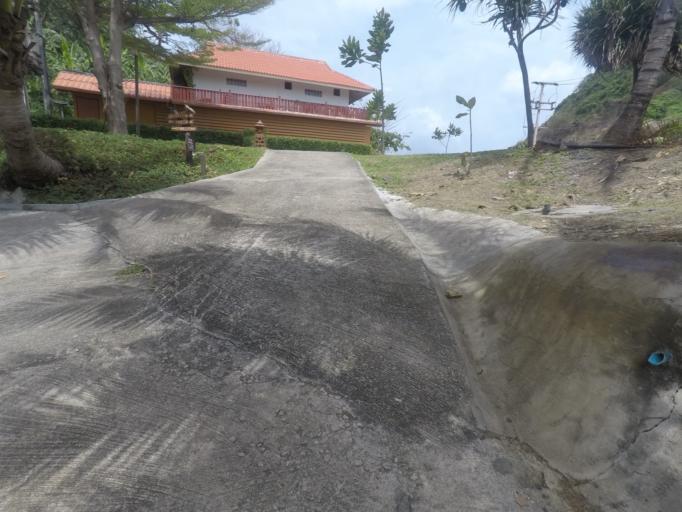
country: TH
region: Phangnga
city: Ban Phru Nai
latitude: 7.7778
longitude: 98.7615
